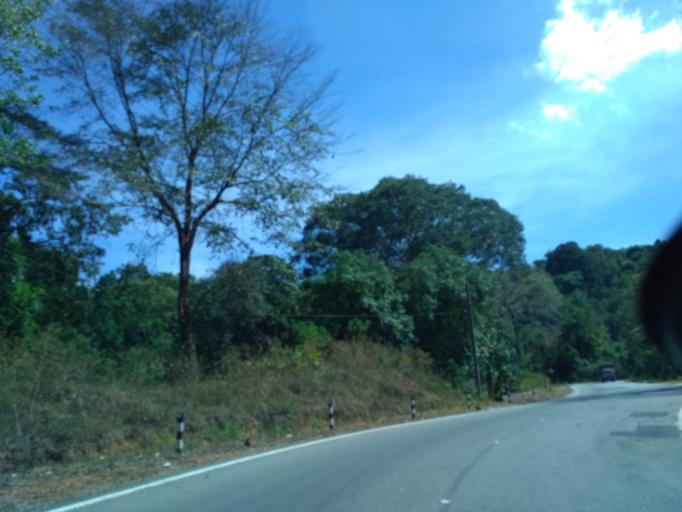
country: IN
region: Karnataka
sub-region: Kodagu
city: Madikeri
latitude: 12.4497
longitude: 75.6404
